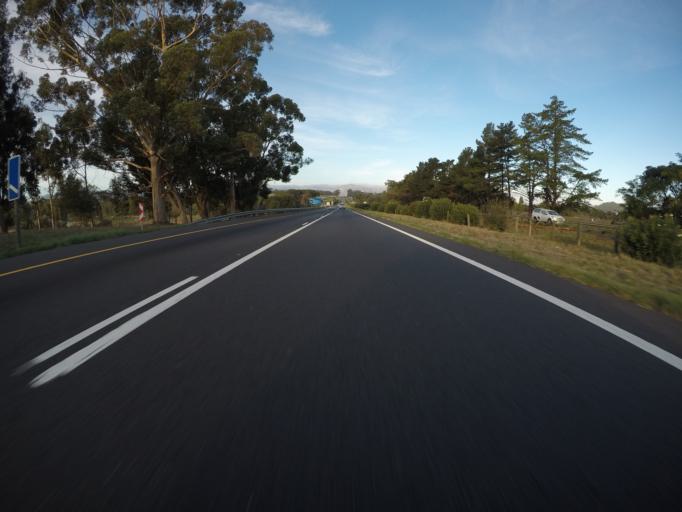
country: ZA
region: Western Cape
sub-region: Cape Winelands District Municipality
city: Paarl
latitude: -33.7993
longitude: 18.8658
